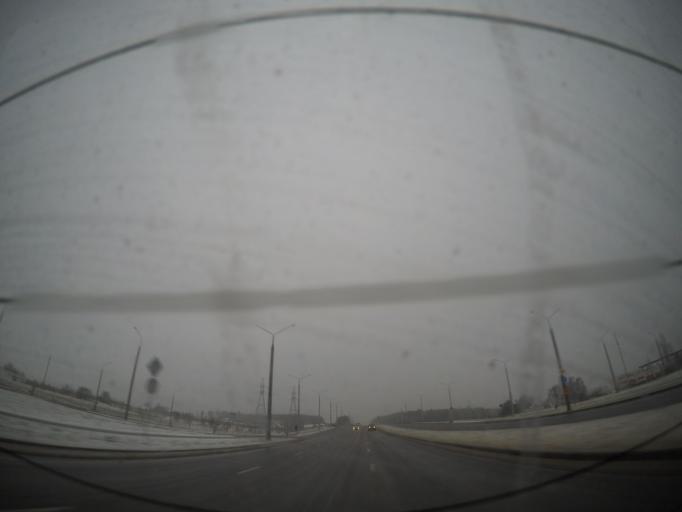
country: BY
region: Grodnenskaya
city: Hrodna
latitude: 53.6365
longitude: 23.8115
